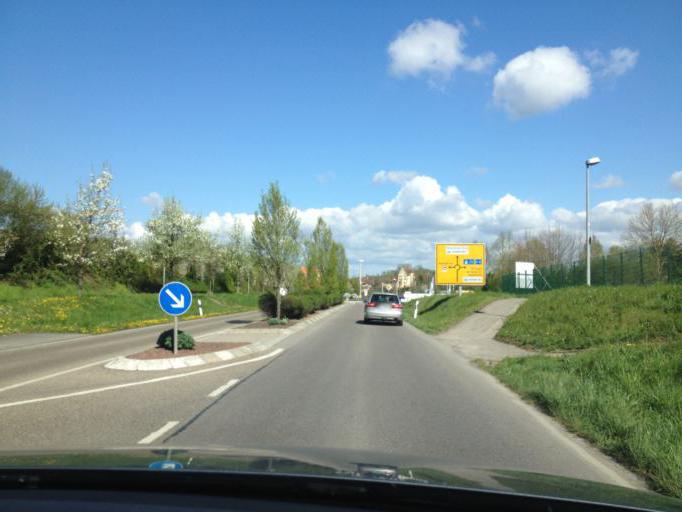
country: DE
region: Baden-Wuerttemberg
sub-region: Regierungsbezirk Stuttgart
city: Neuenstadt am Kocher
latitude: 49.2360
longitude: 9.3440
